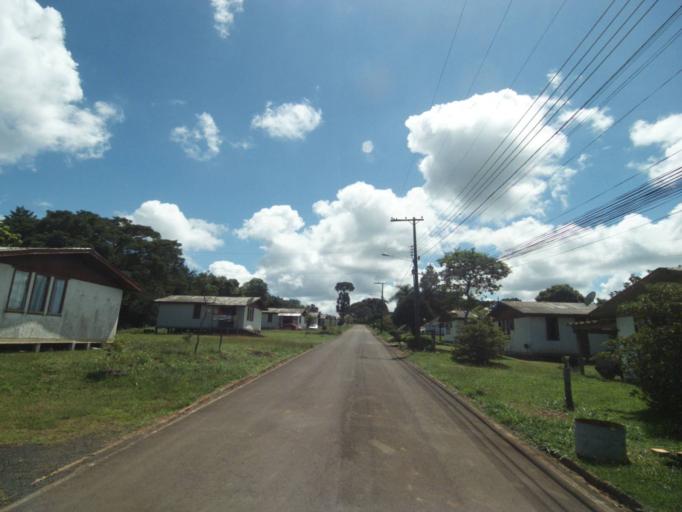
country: BR
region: Parana
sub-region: Chopinzinho
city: Chopinzinho
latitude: -25.7955
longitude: -52.0913
